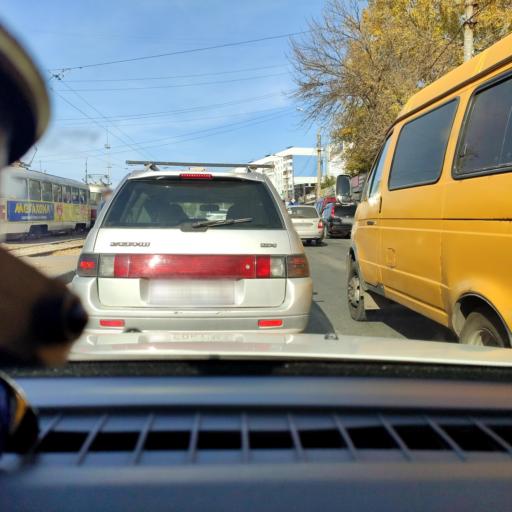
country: RU
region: Samara
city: Samara
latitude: 53.2422
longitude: 50.2113
